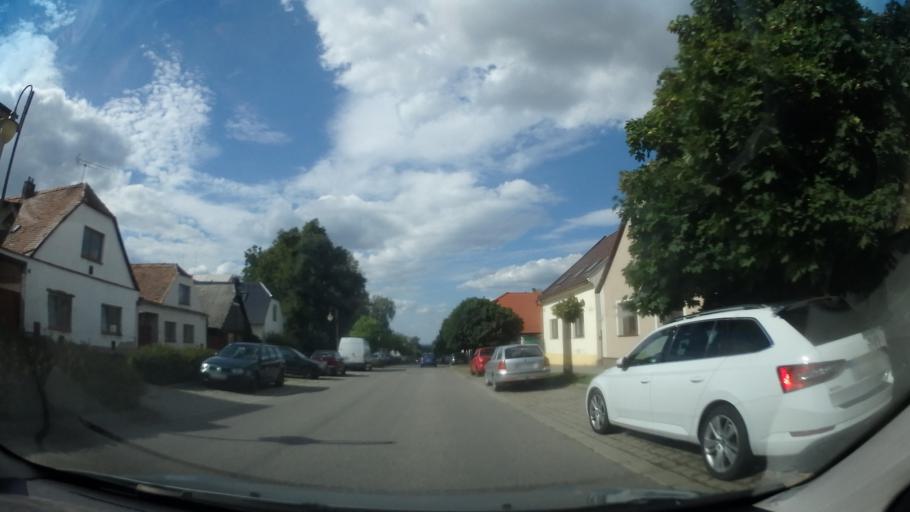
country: CZ
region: Vysocina
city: Golcuv Jenikov
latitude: 49.8196
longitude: 15.4755
